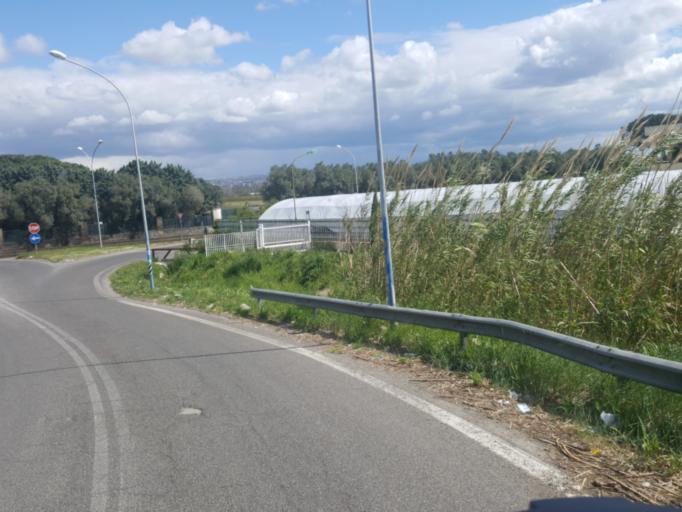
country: IT
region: Campania
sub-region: Provincia di Napoli
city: Masseria Vecchia Ovest
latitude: 40.9315
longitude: 14.0788
